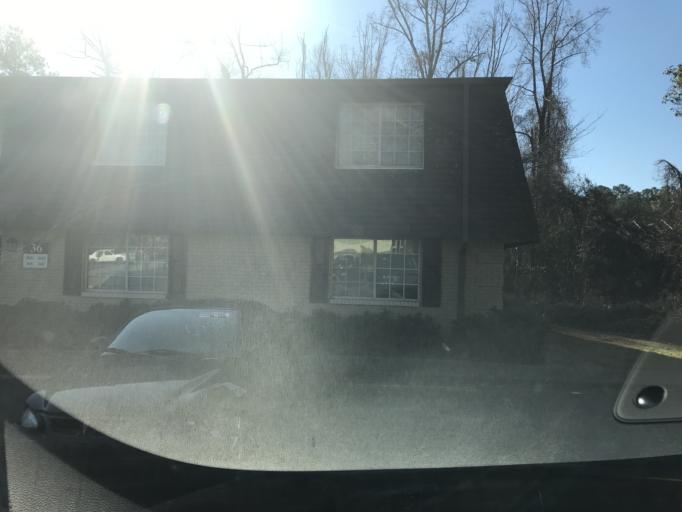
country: US
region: Georgia
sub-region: Clayton County
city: Morrow
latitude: 33.5692
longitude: -84.3650
